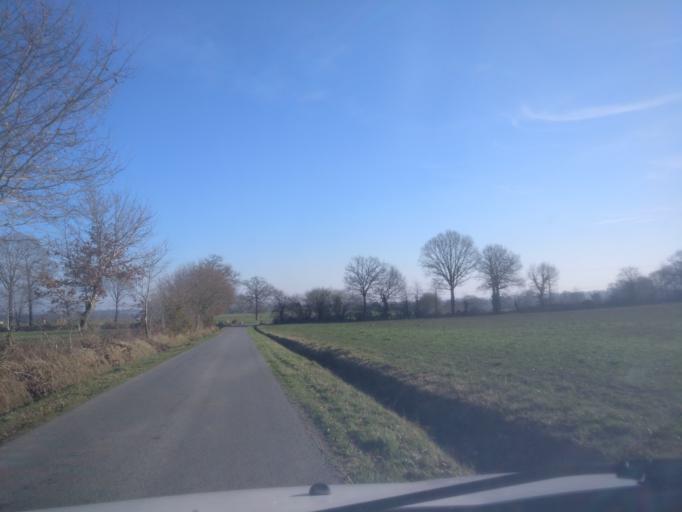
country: FR
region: Brittany
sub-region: Departement d'Ille-et-Vilaine
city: Livre-sur-Changeon
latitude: 48.2437
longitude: -1.3559
